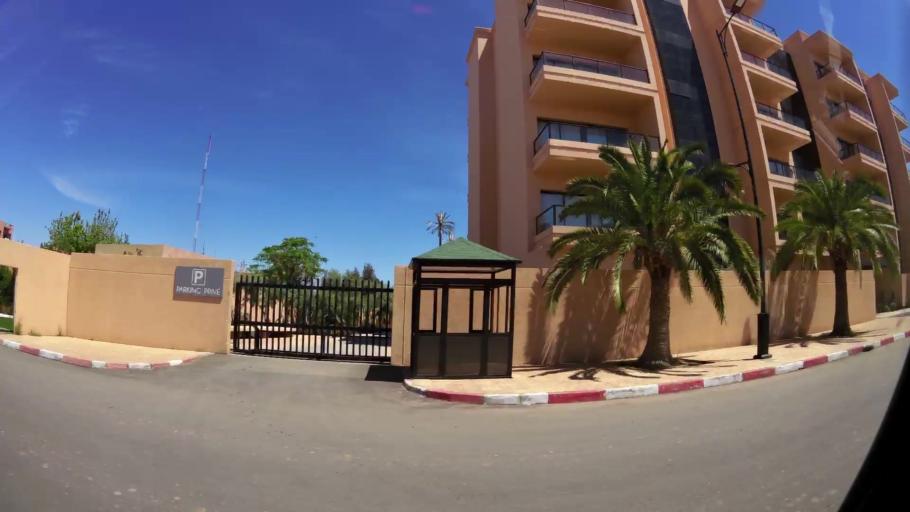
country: MA
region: Marrakech-Tensift-Al Haouz
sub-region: Marrakech
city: Marrakesh
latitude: 31.6253
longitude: -8.0170
